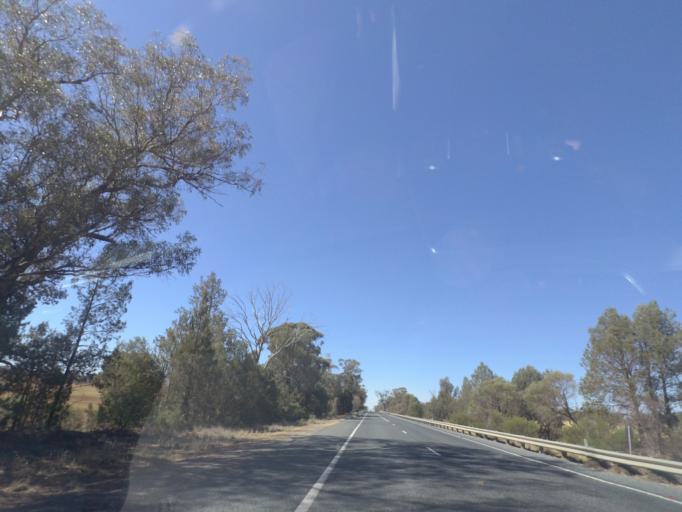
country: AU
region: New South Wales
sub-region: Bland
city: West Wyalong
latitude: -34.1636
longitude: 147.1163
